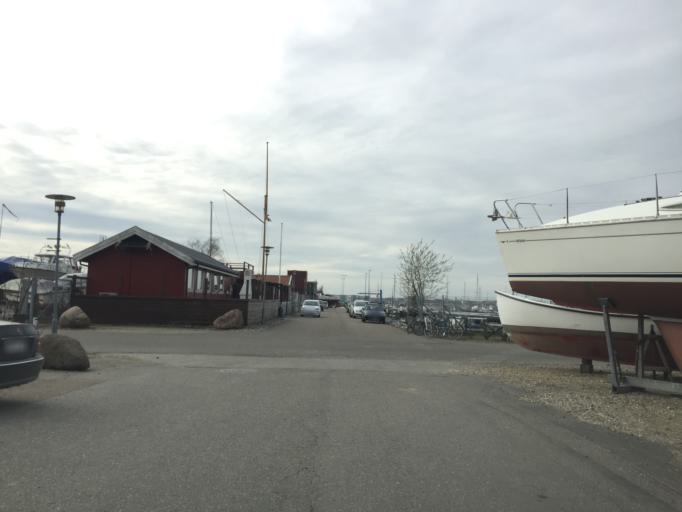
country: DK
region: Capital Region
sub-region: Gentofte Kommune
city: Charlottenlund
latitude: 55.7229
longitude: 12.6067
